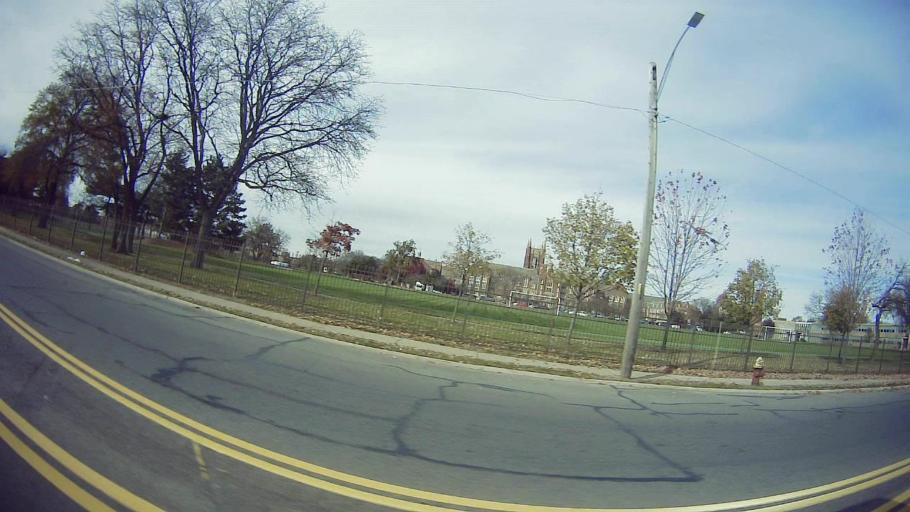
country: US
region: Michigan
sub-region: Wayne County
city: Highland Park
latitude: 42.3728
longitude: -83.1106
